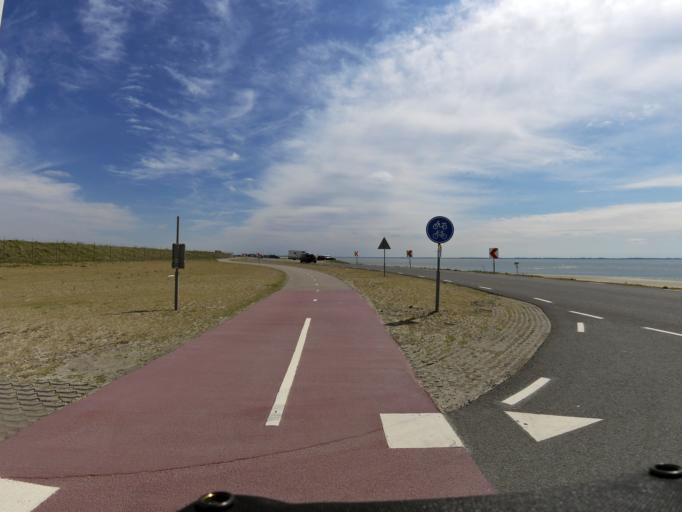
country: NL
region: South Holland
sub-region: Gemeente Goeree-Overflakkee
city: Goedereede
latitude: 51.9202
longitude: 3.9915
